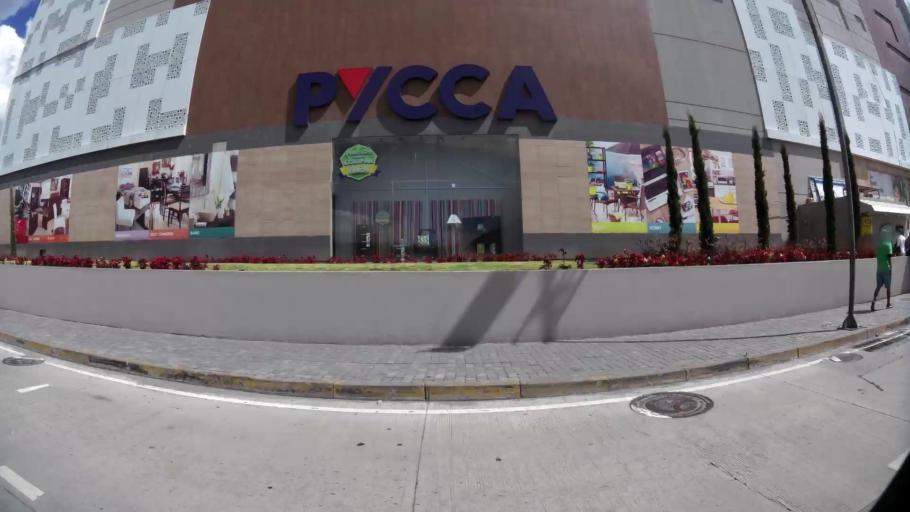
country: EC
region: Pichincha
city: Quito
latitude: -0.1026
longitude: -78.4895
